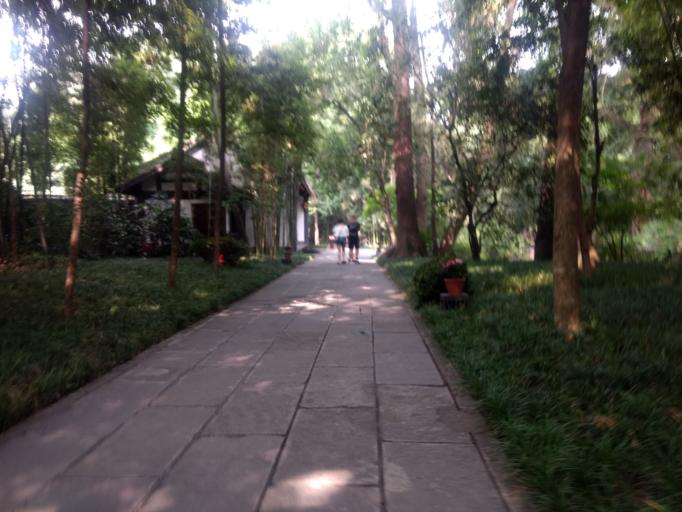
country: CN
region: Sichuan
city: Chengdu
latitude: 30.6619
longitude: 104.0245
